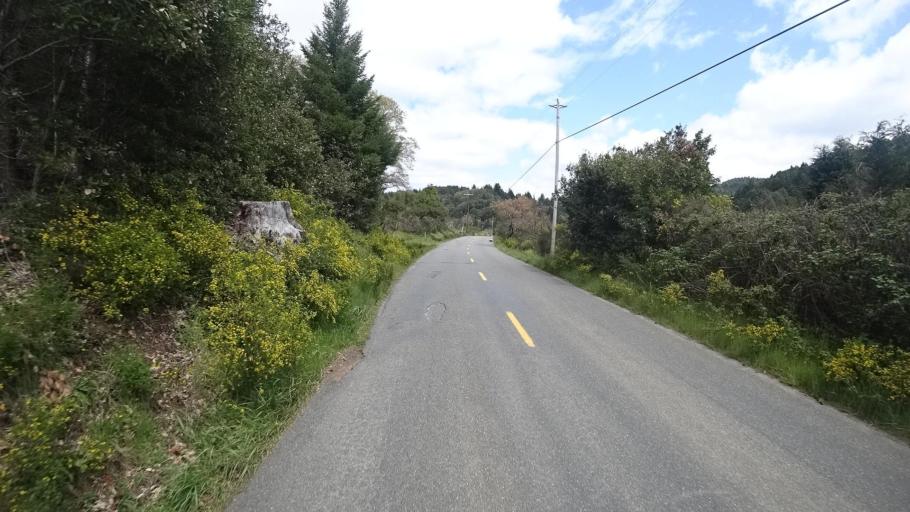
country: US
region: California
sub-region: Humboldt County
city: Redway
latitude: 40.0657
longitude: -123.9629
